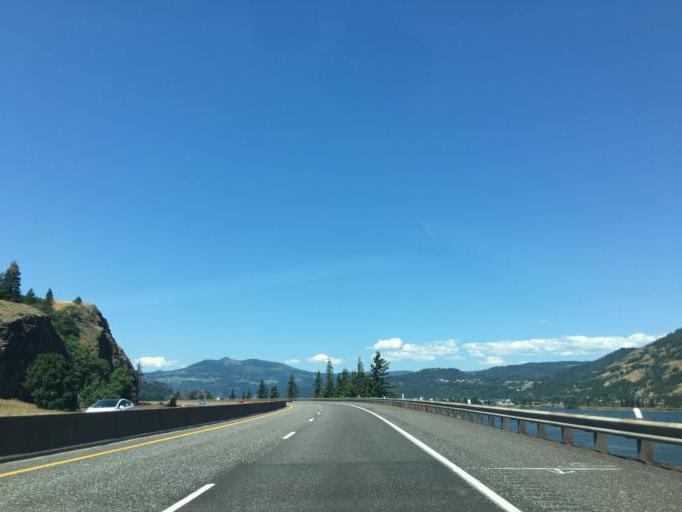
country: US
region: Washington
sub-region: Klickitat County
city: White Salmon
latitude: 45.6946
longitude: -121.4451
